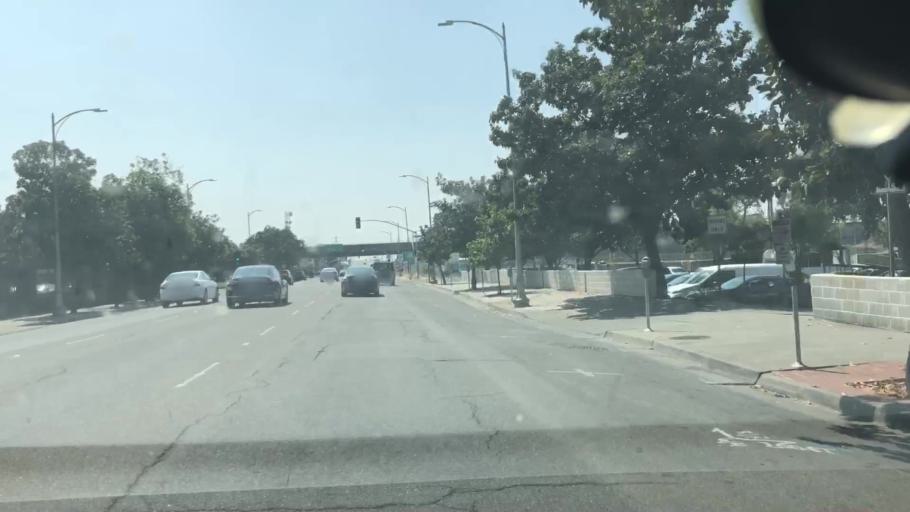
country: US
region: California
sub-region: San Joaquin County
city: Stockton
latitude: 37.9522
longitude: -121.2911
